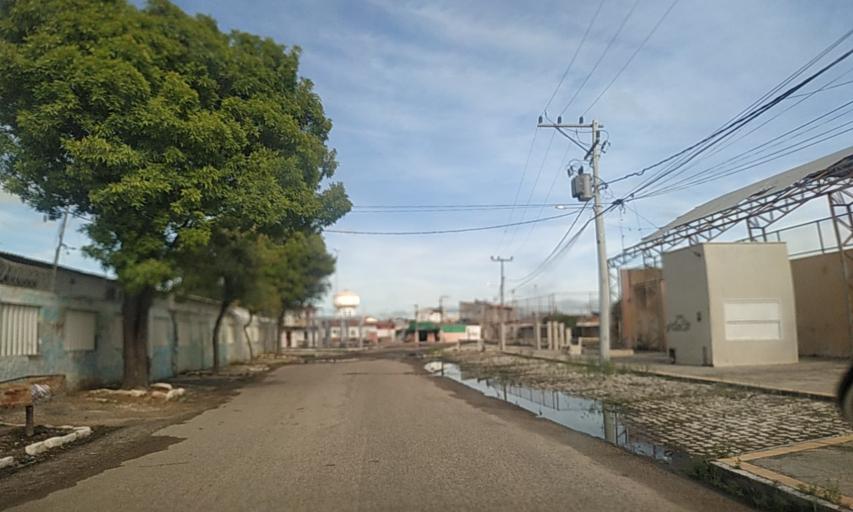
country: BR
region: Rio Grande do Norte
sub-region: Areia Branca
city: Areia Branca
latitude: -4.9538
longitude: -37.1266
